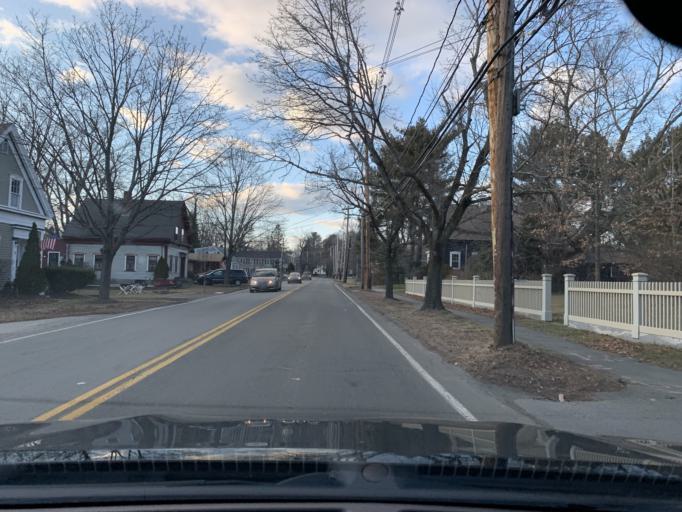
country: US
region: Massachusetts
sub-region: Essex County
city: Danvers
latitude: 42.5660
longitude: -70.9632
